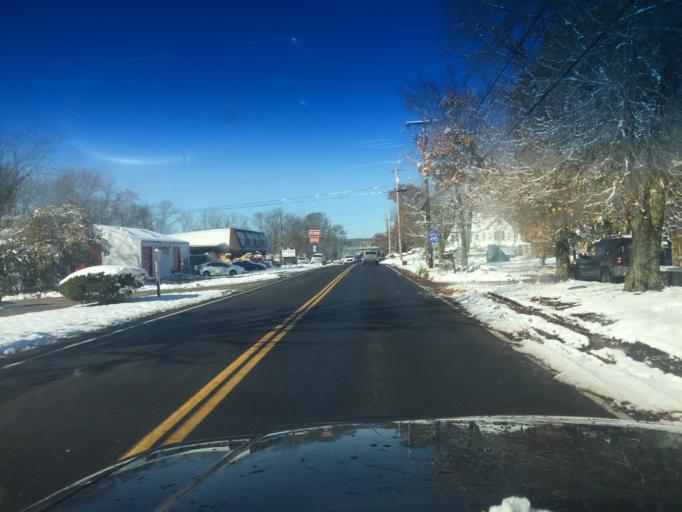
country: US
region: Massachusetts
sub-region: Worcester County
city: Milford
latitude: 42.1470
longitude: -71.4789
